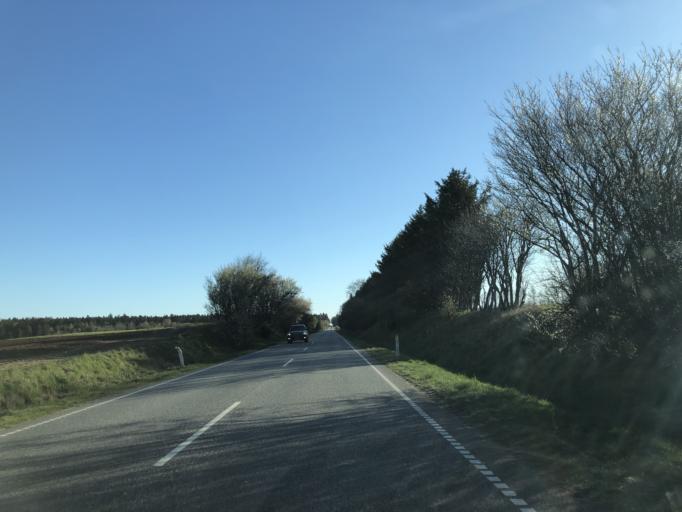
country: DK
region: Central Jutland
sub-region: Herning Kommune
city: Avlum
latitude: 56.2745
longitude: 8.8118
